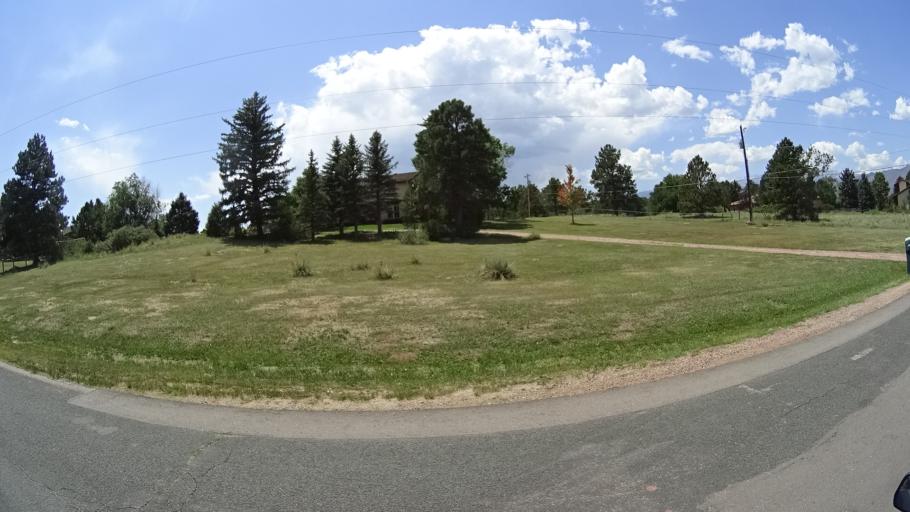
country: US
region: Colorado
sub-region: El Paso County
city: Air Force Academy
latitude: 38.9368
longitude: -104.8044
